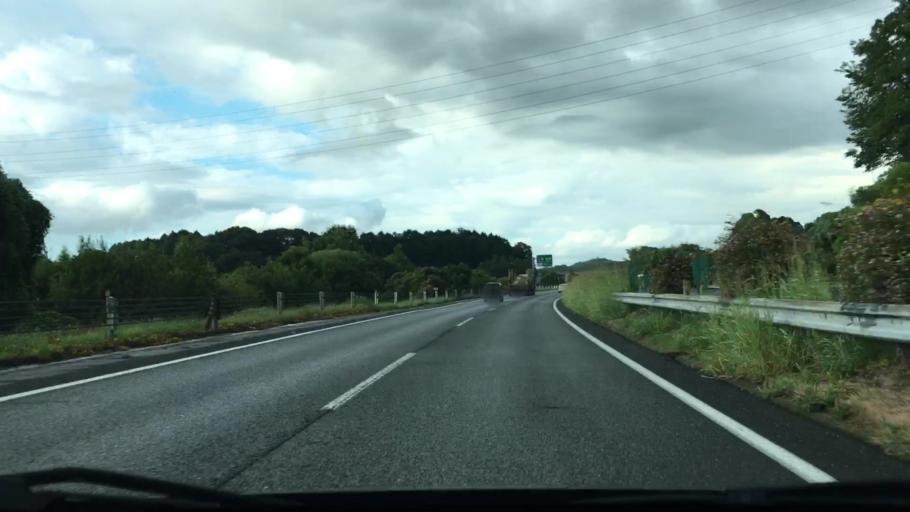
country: JP
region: Fukuoka
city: Koga
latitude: 33.7070
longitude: 130.4863
